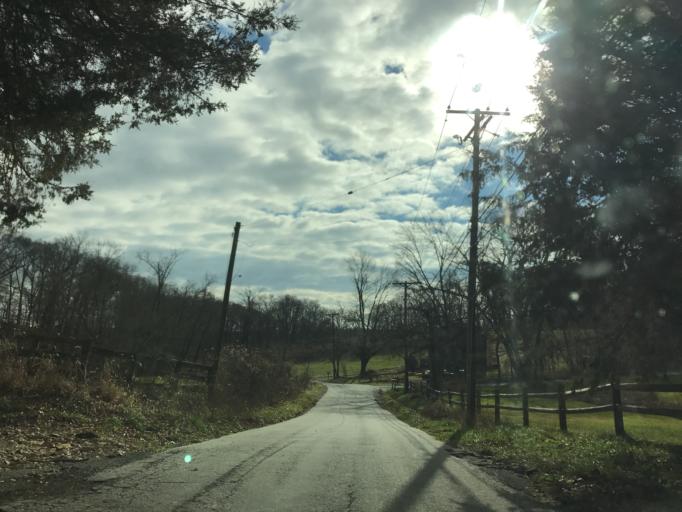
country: US
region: Maryland
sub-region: Baltimore County
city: Perry Hall
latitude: 39.4765
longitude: -76.5150
